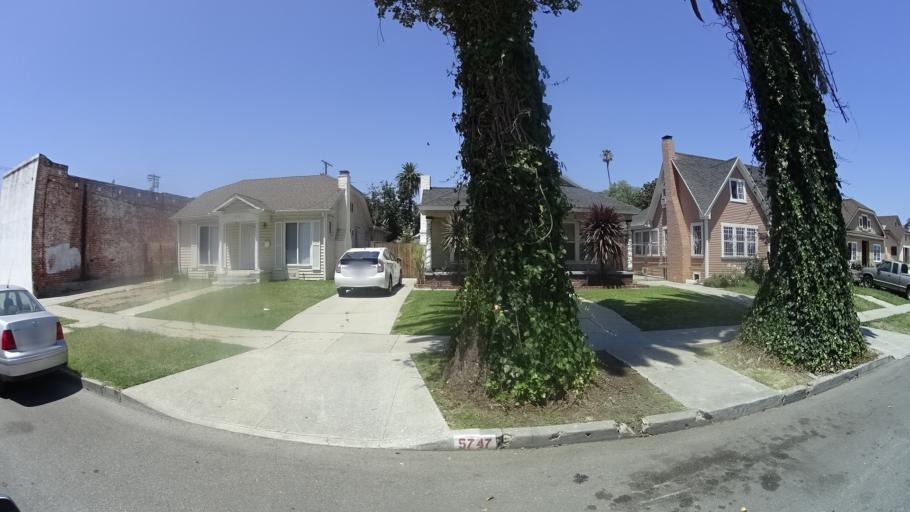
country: US
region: California
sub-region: Los Angeles County
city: View Park-Windsor Hills
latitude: 33.9896
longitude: -118.3237
